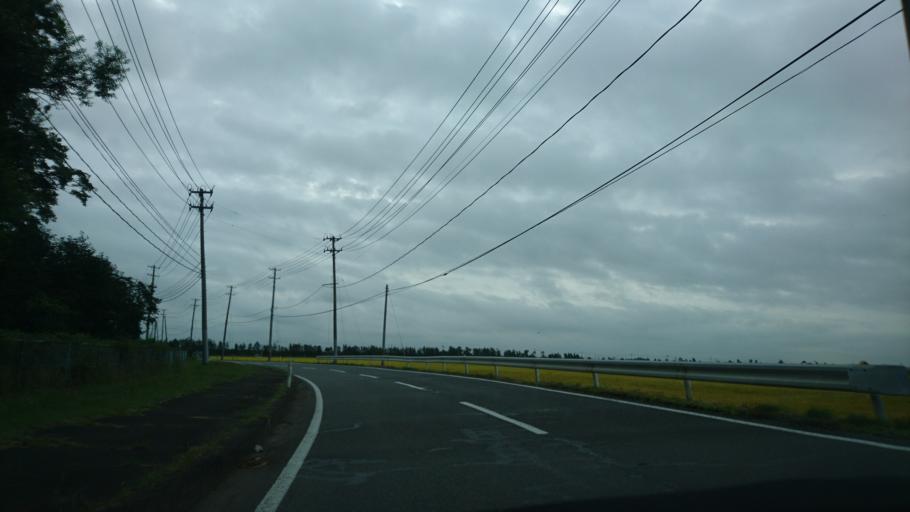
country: JP
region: Iwate
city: Ichinoseki
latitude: 38.8051
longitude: 141.0880
